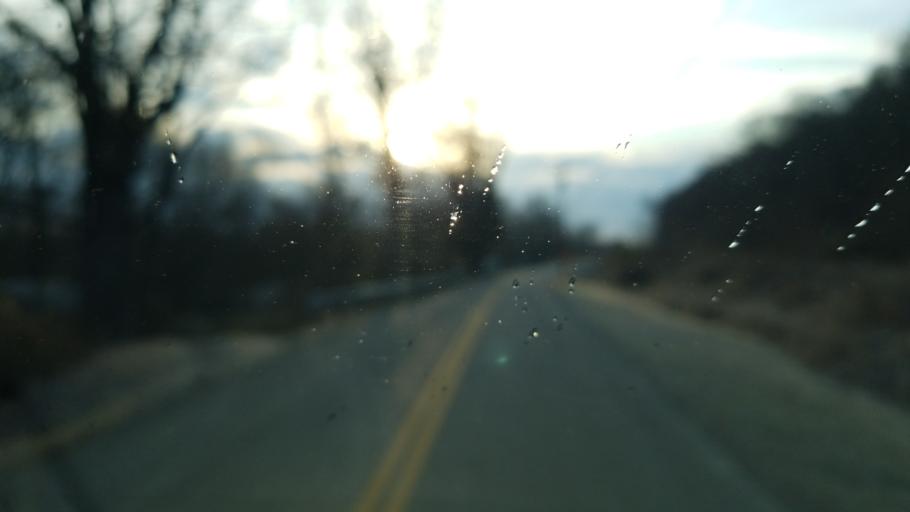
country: US
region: Ohio
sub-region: Ross County
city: Chillicothe
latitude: 39.2811
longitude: -82.9344
